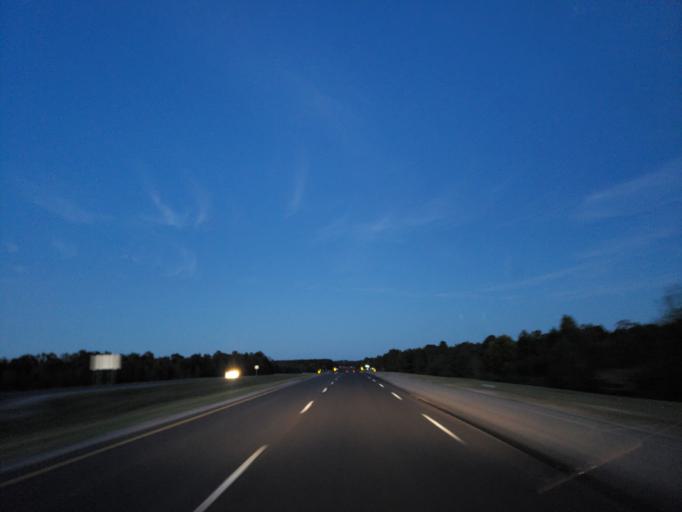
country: US
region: Mississippi
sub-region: Clarke County
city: Quitman
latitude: 31.9798
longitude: -88.7197
